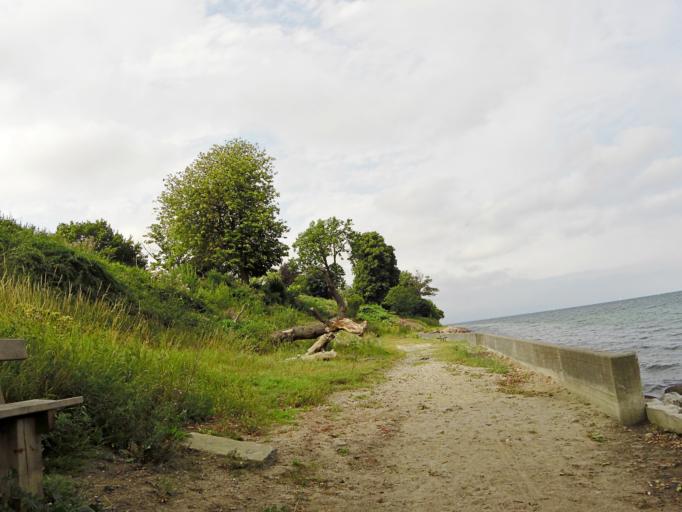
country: DK
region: Capital Region
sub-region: Gentofte Kommune
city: Charlottenlund
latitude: 55.7963
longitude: 12.5900
